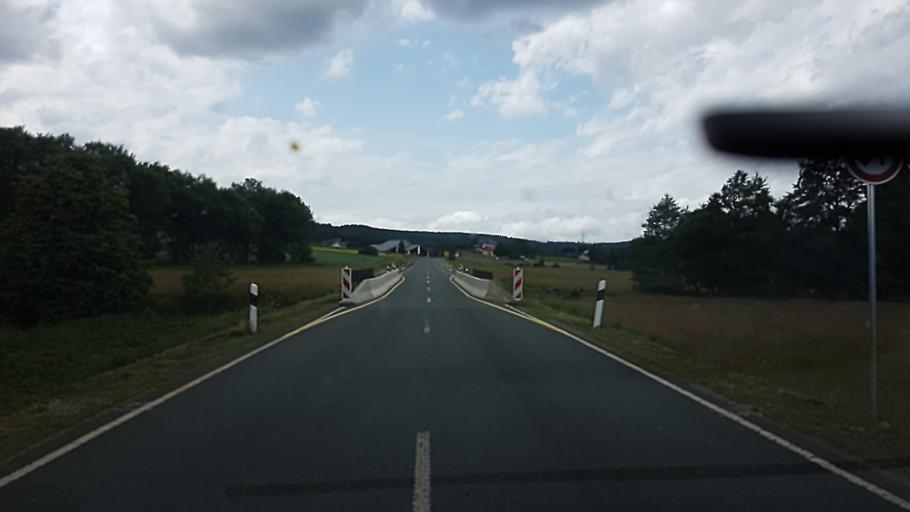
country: DE
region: Bavaria
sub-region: Upper Franconia
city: Mehlmeisel
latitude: 49.9829
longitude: 11.8638
